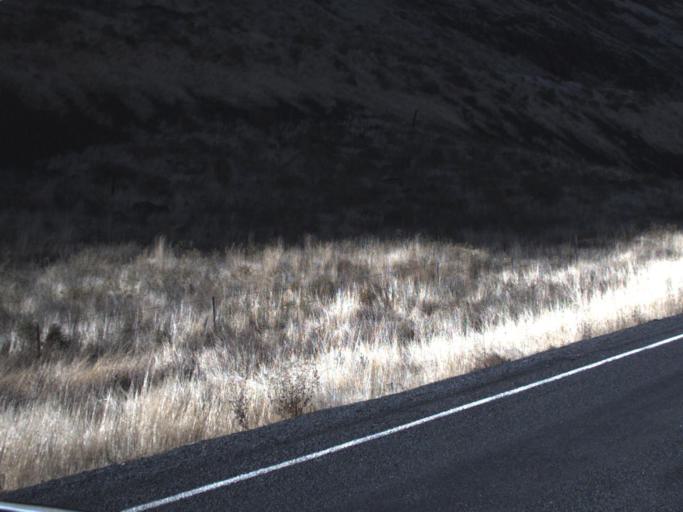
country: US
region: Washington
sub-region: Franklin County
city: Connell
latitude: 46.6034
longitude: -118.5509
